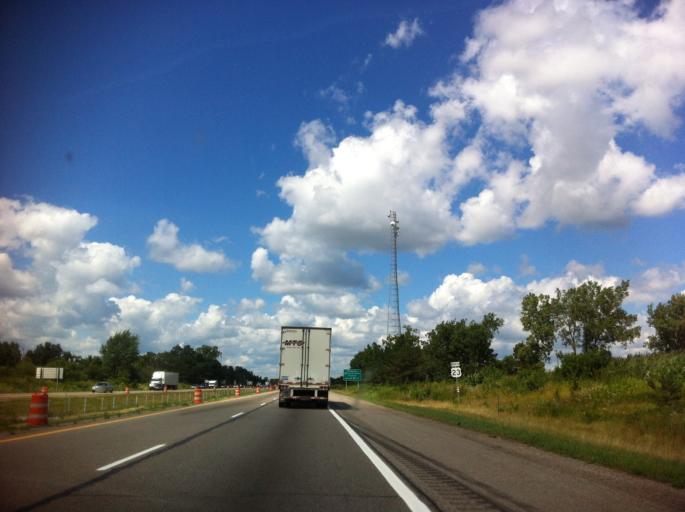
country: US
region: Michigan
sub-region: Washtenaw County
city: Ypsilanti
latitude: 42.2119
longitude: -83.6850
